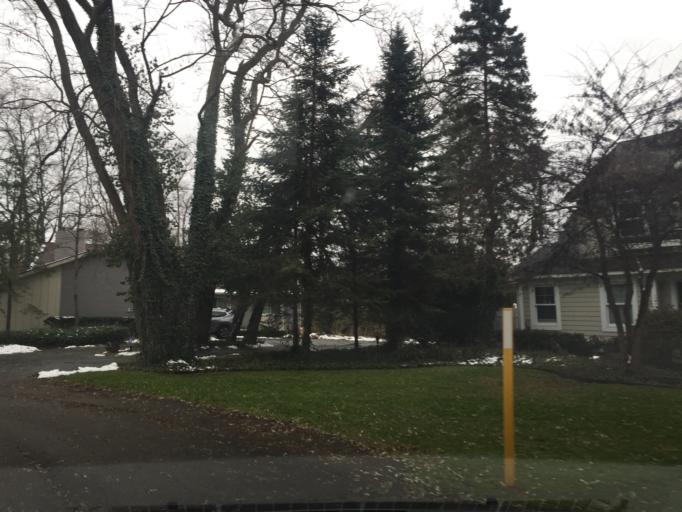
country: US
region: Michigan
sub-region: Oakland County
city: Franklin
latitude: 42.5536
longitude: -83.2902
